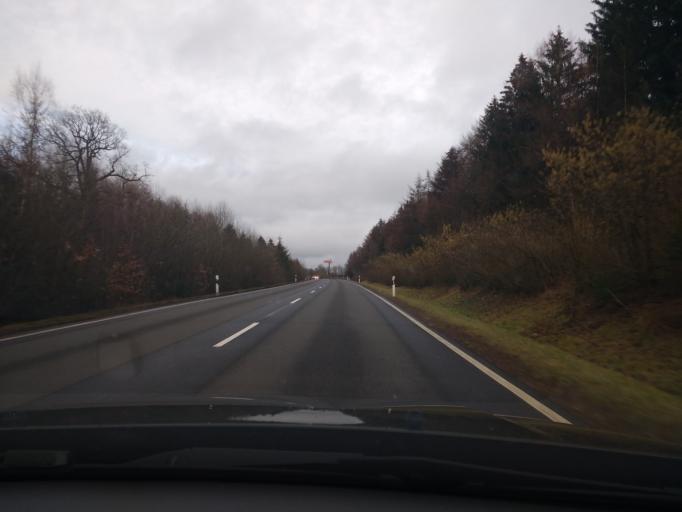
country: DE
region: Rheinland-Pfalz
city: Hermeskeil
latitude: 49.6786
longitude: 6.9446
